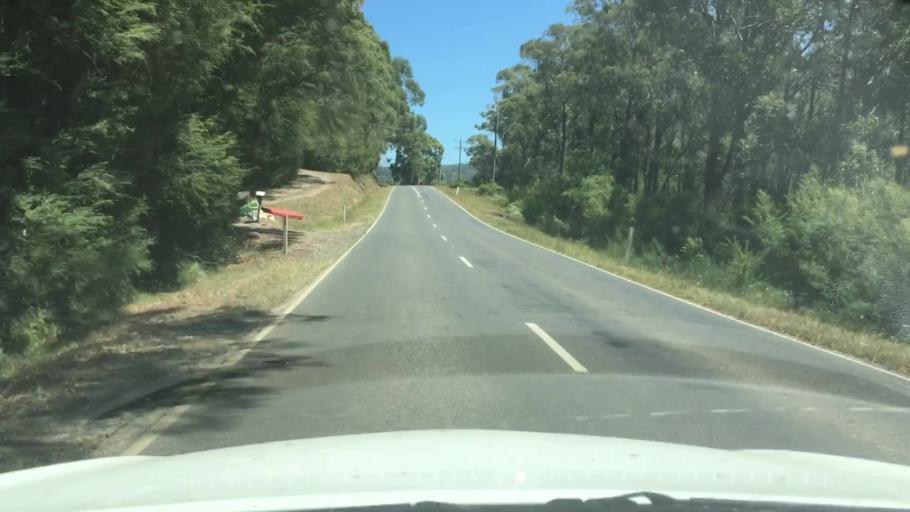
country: AU
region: Victoria
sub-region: Yarra Ranges
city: Millgrove
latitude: -37.7263
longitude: 145.7519
